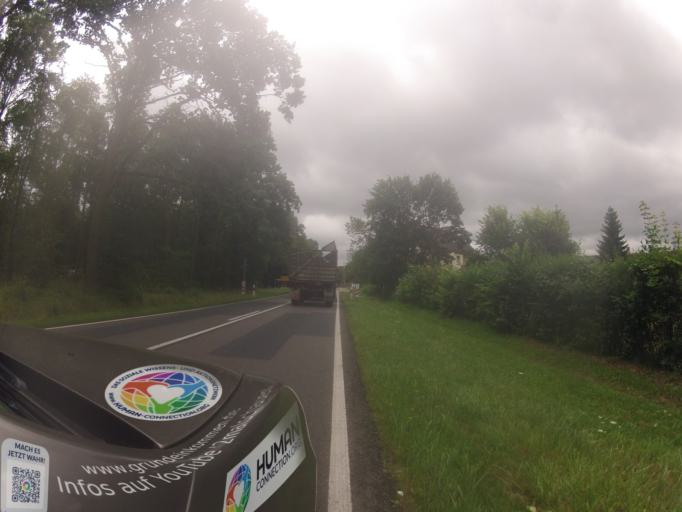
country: DE
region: Mecklenburg-Vorpommern
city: Jatznick
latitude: 53.6032
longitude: 13.9394
